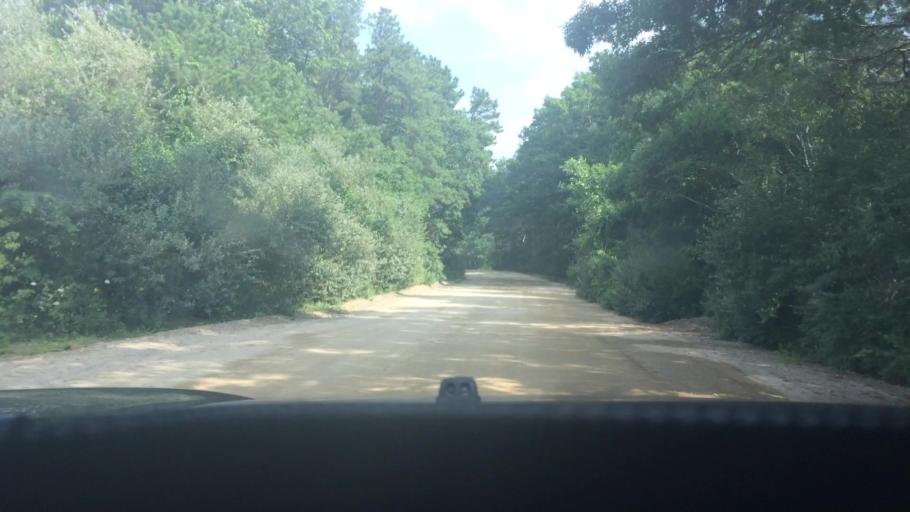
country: US
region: Massachusetts
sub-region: Barnstable County
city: Forestdale
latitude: 41.7244
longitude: -70.4859
